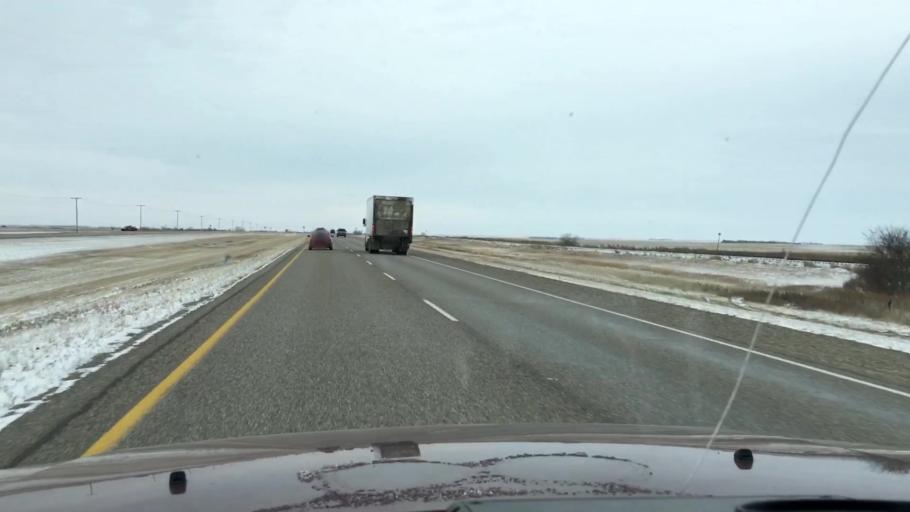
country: CA
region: Saskatchewan
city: Watrous
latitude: 51.1826
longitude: -105.9412
